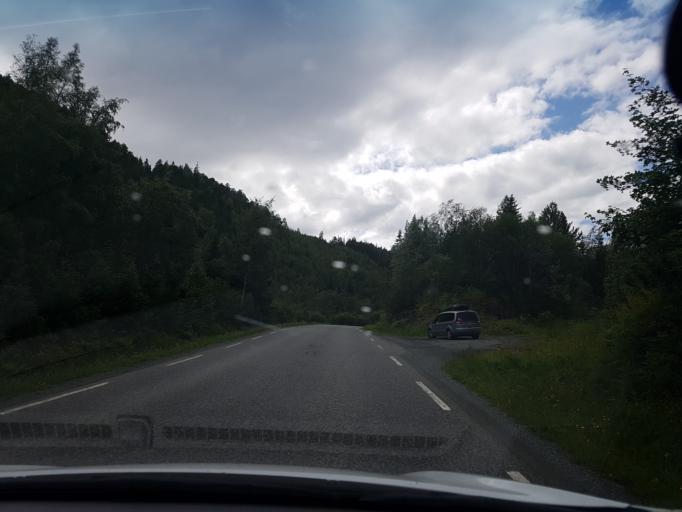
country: NO
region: Nord-Trondelag
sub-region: Stjordal
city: Stjordalshalsen
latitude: 63.6080
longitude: 10.9469
